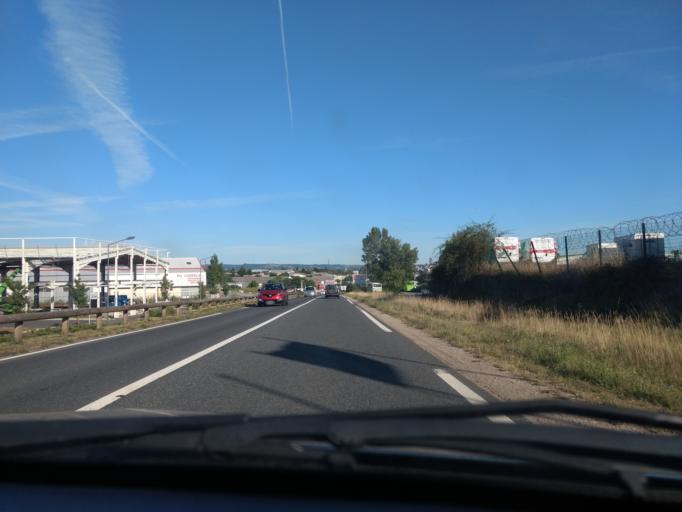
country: FR
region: Midi-Pyrenees
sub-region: Departement de l'Aveyron
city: Olemps
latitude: 44.3767
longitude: 2.5404
